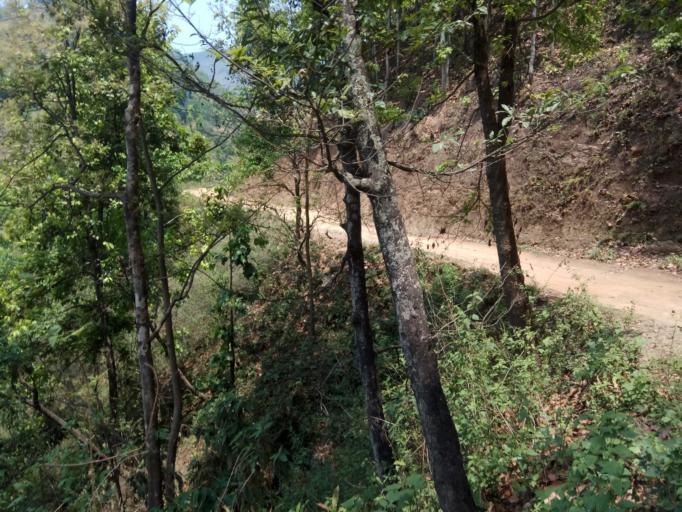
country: NP
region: Central Region
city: Kirtipur
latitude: 27.8937
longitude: 85.0889
